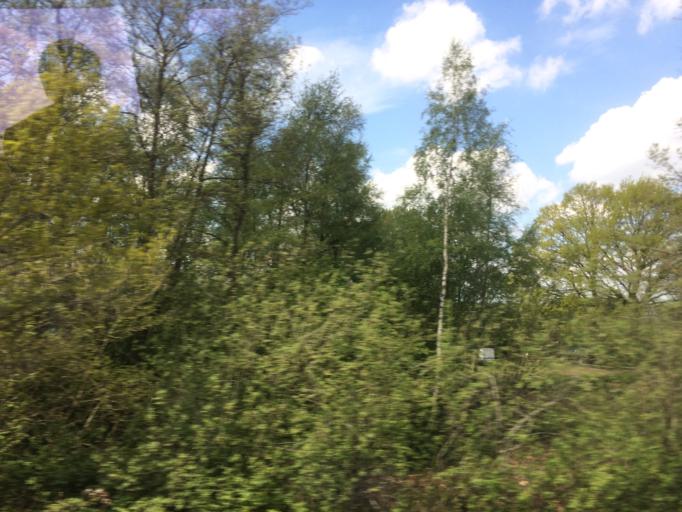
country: DE
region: Schleswig-Holstein
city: Wulfsmoor
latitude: 53.9255
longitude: 9.7422
